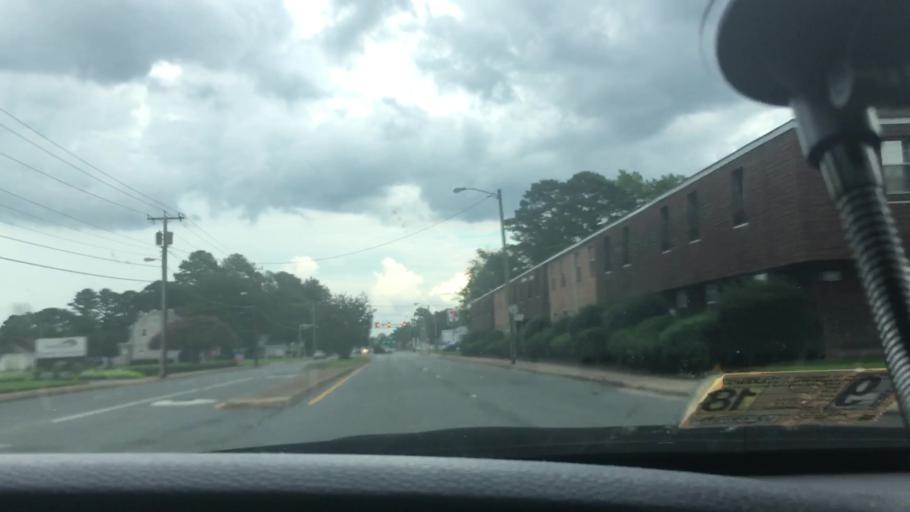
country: US
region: Virginia
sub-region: City of Portsmouth
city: Portsmouth Heights
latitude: 36.8187
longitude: -76.3753
